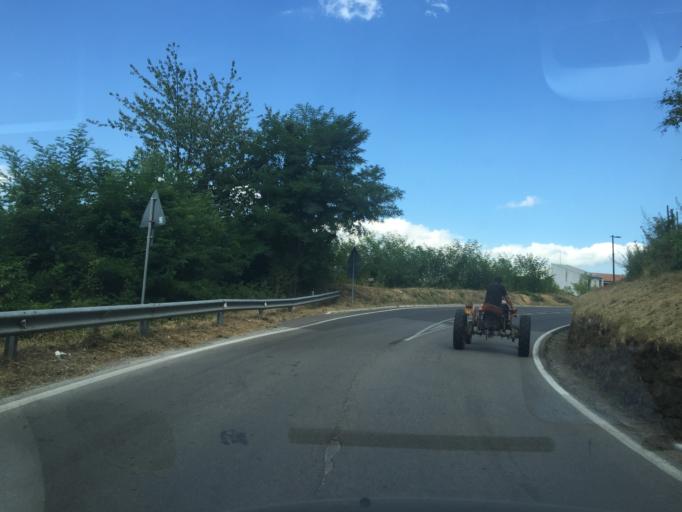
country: IT
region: Tuscany
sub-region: Provincia di Lucca
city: Castelnuovo di Garfagnana
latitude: 44.1174
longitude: 10.3960
